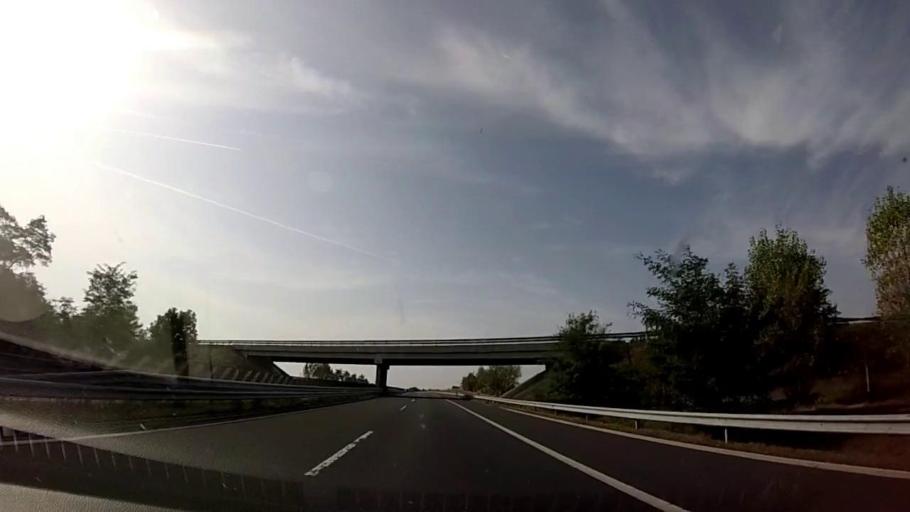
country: HU
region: Somogy
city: Balatonbereny
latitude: 46.6155
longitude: 17.2600
